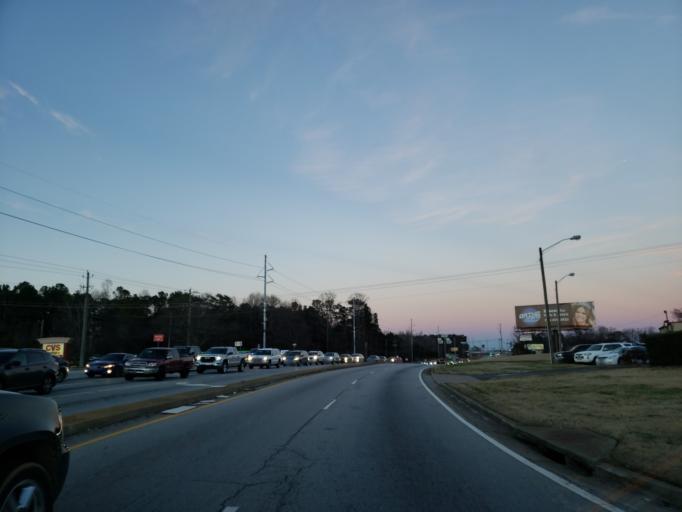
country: US
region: Georgia
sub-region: Paulding County
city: Hiram
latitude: 33.9093
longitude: -84.7785
